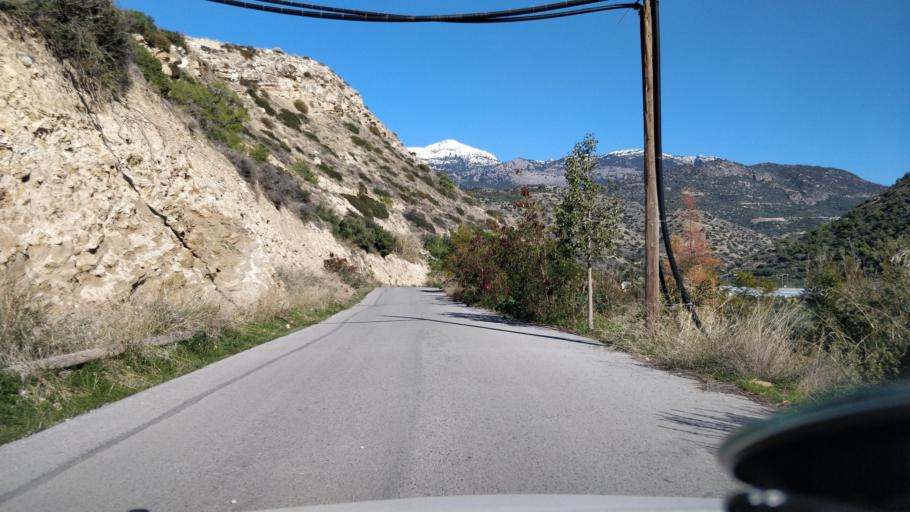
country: GR
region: Crete
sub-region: Nomos Lasithiou
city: Gra Liyia
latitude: 34.9887
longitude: 25.4814
